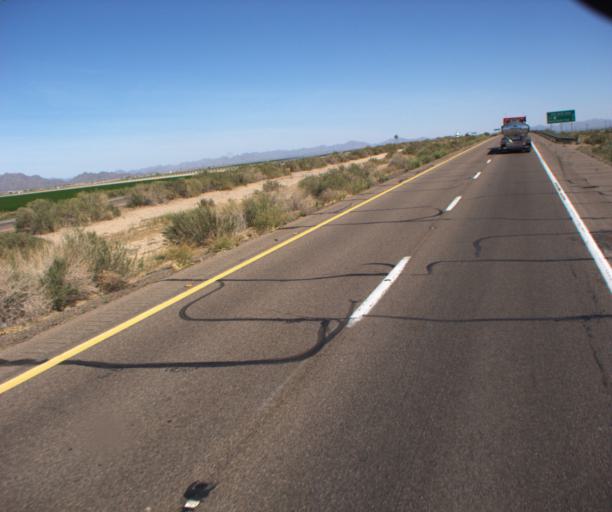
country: US
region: Arizona
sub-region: Maricopa County
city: Gila Bend
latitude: 32.9317
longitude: -112.8076
